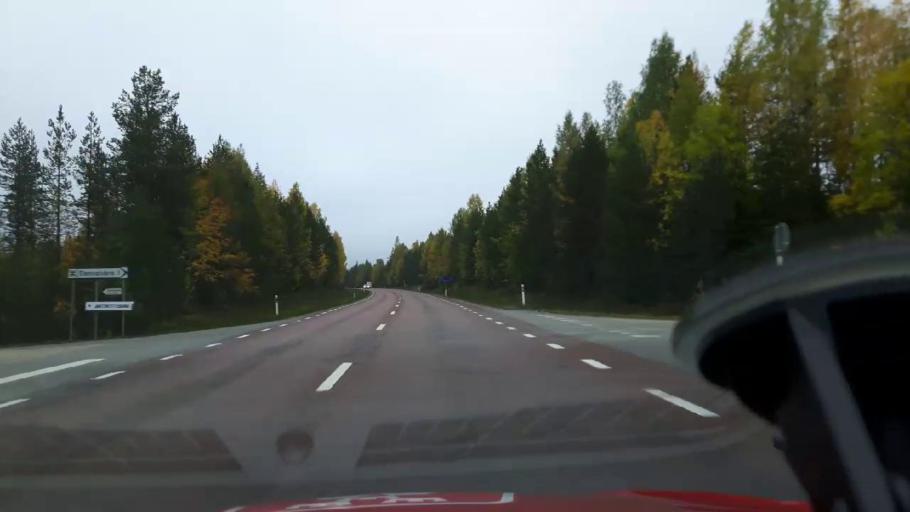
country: SE
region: Jaemtland
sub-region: Bergs Kommun
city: Hoverberg
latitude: 62.6347
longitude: 14.3675
